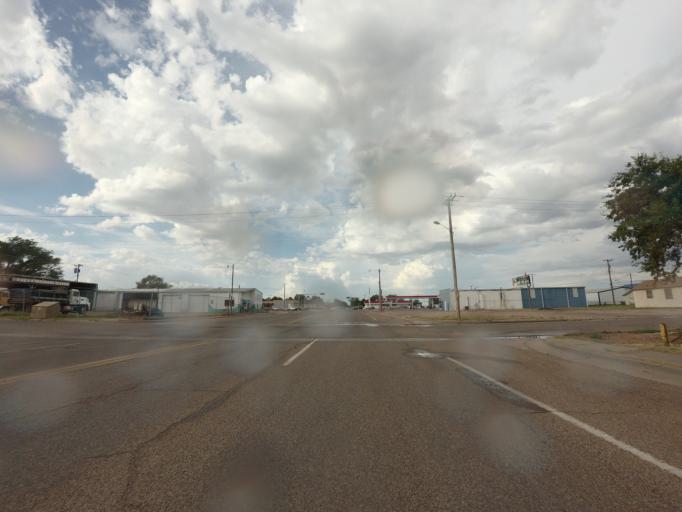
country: US
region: New Mexico
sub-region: Curry County
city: Clovis
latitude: 34.4037
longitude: -103.2204
